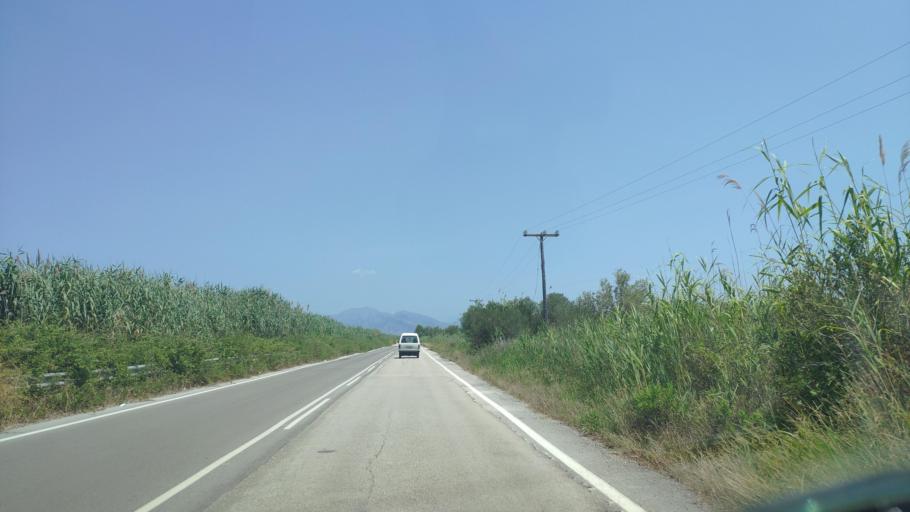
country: GR
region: Epirus
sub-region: Nomos Artas
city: Aneza
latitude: 39.0512
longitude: 20.8628
